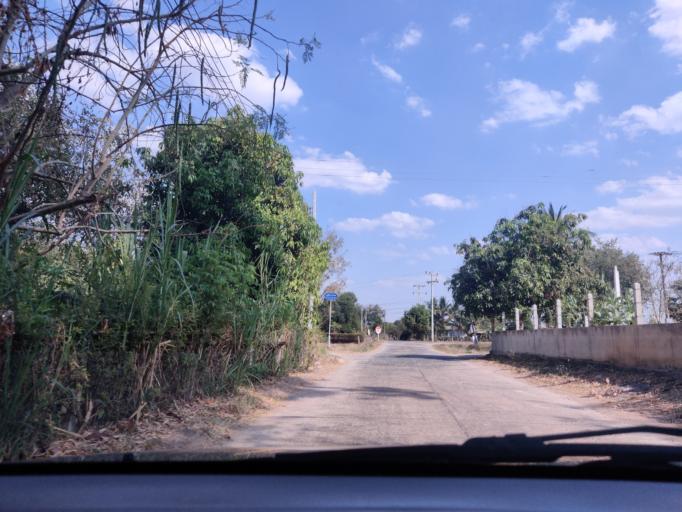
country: TH
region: Sisaket
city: Si Sa Ket
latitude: 15.0654
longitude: 104.3534
